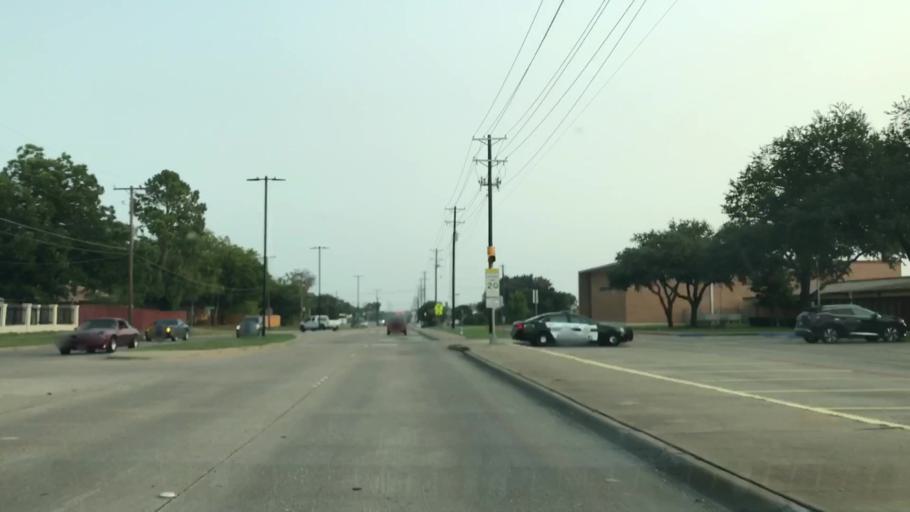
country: US
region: Texas
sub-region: Dallas County
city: Garland
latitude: 32.8834
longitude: -96.6310
